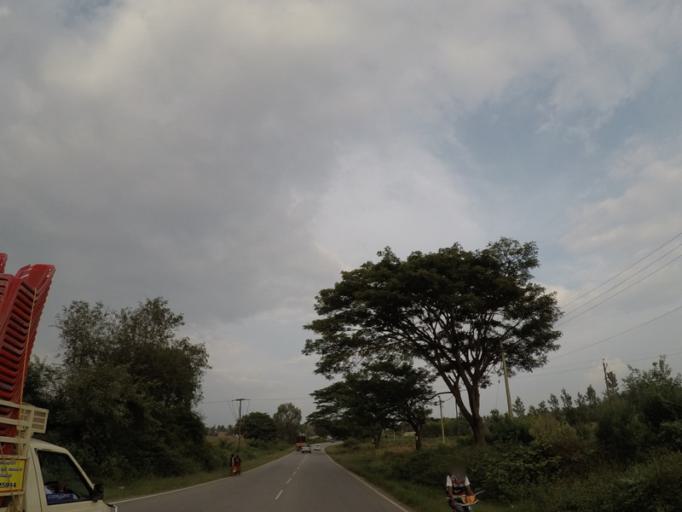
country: IN
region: Karnataka
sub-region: Hassan
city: Belur
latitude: 13.1580
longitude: 75.9292
